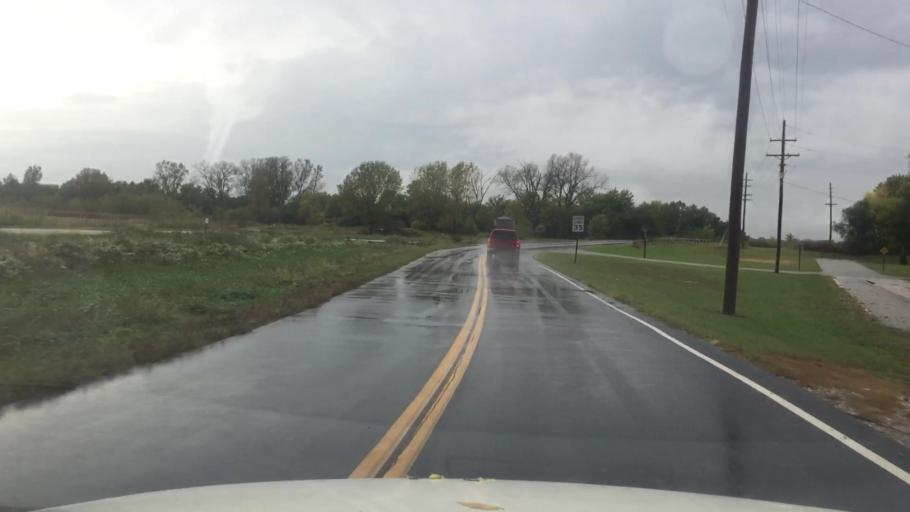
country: US
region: Missouri
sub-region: Boone County
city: Columbia
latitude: 38.8860
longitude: -92.4481
